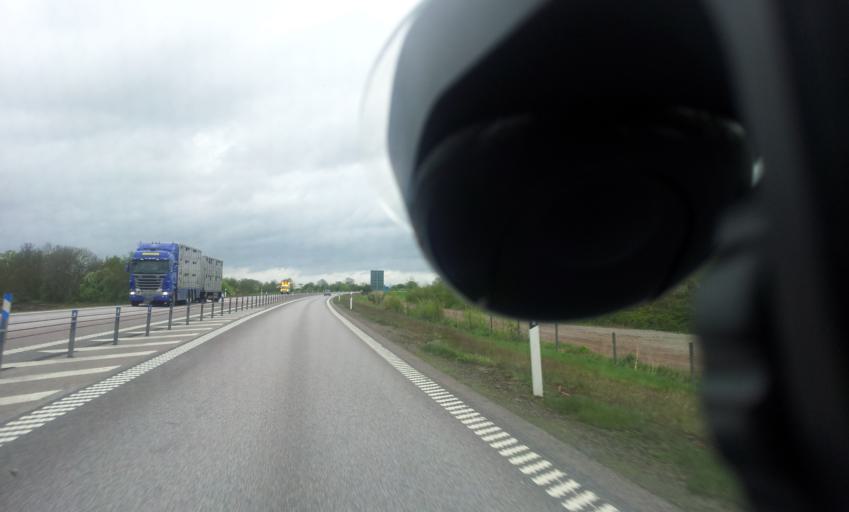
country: SE
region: Kalmar
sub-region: Kalmar Kommun
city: Ljungbyholm
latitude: 56.6116
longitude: 16.1408
